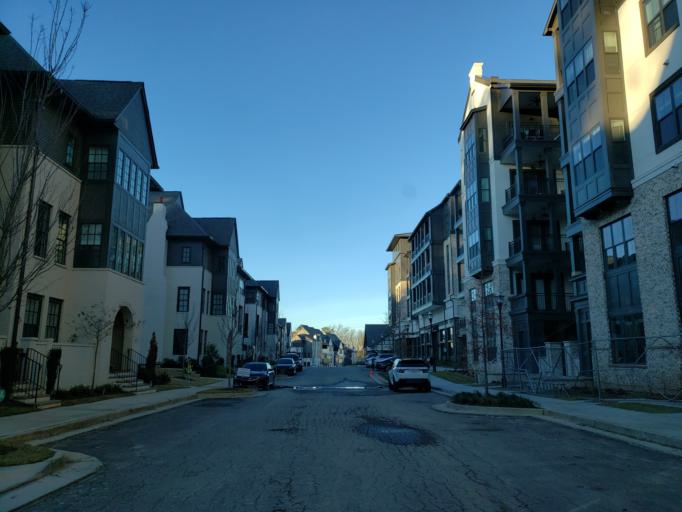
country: US
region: Georgia
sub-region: Fulton County
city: Sandy Springs
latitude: 33.9335
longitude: -84.3654
